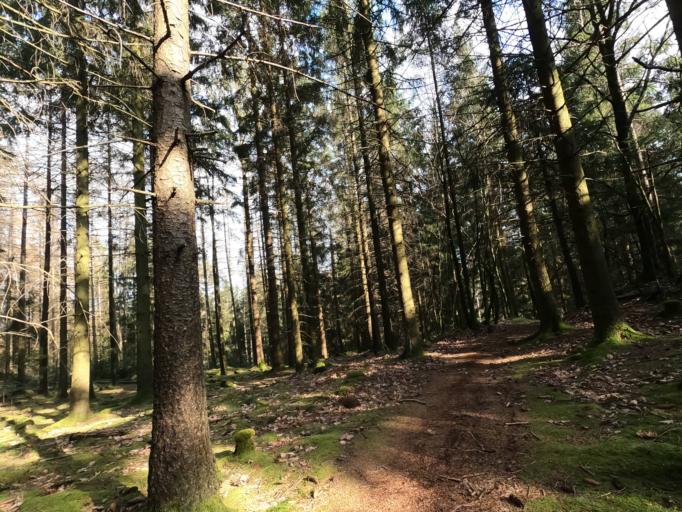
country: DE
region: North Rhine-Westphalia
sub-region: Regierungsbezirk Arnsberg
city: Herscheid
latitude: 51.1761
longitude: 7.7571
